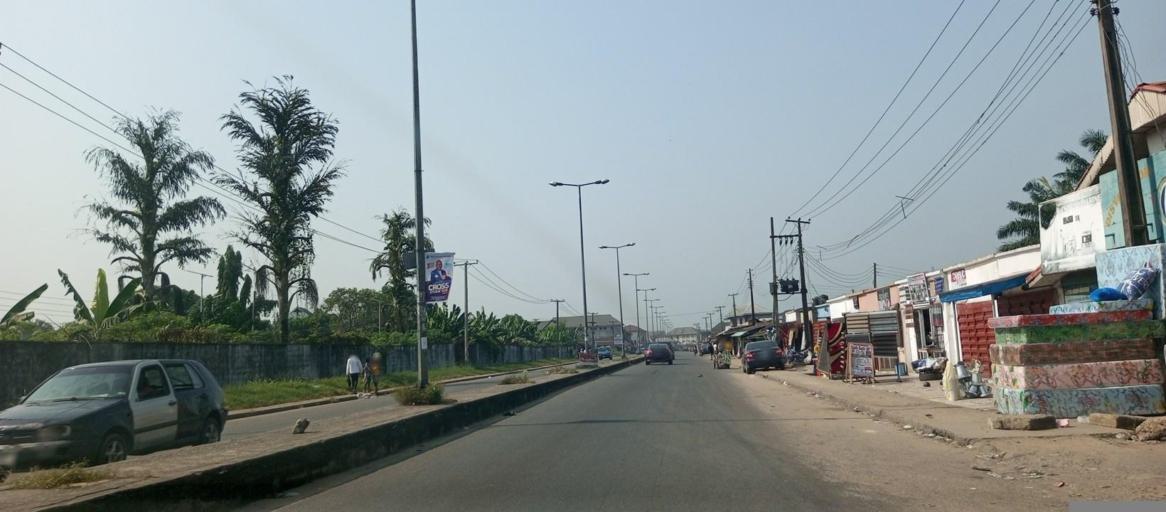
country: NG
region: Rivers
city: Emuoha
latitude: 4.8932
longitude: 6.9056
